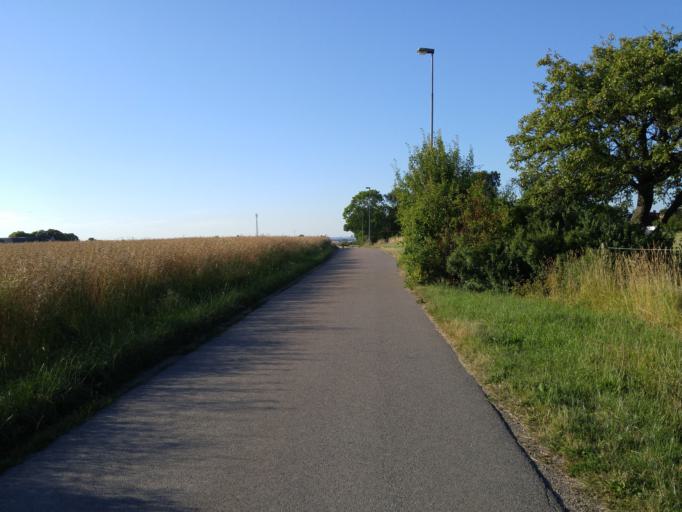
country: SE
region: Skane
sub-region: Lunds Kommun
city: Lund
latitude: 55.7347
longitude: 13.1933
